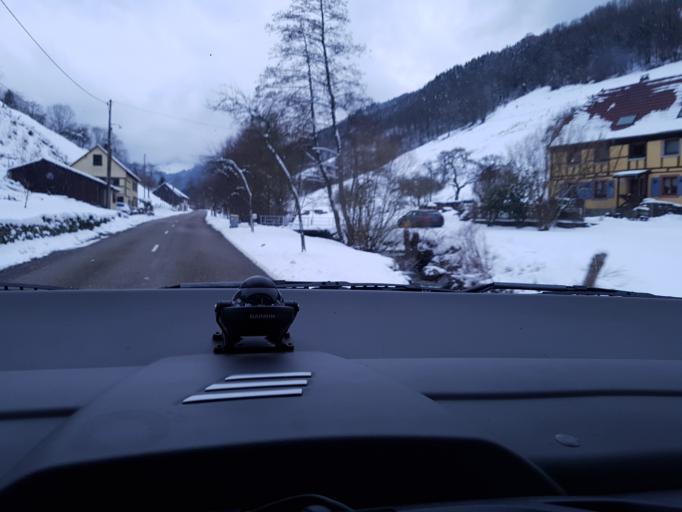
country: FR
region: Alsace
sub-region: Departement du Haut-Rhin
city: Sainte-Marie-aux-Mines
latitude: 48.2281
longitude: 7.1533
